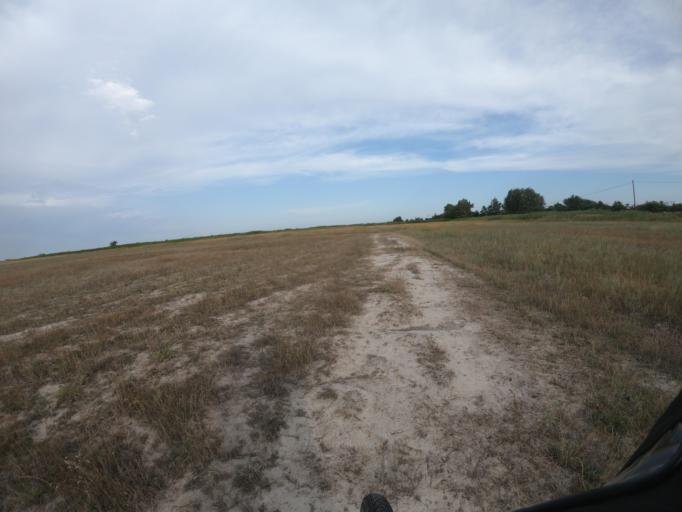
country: HU
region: Hajdu-Bihar
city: Hortobagy
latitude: 47.6077
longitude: 21.0527
